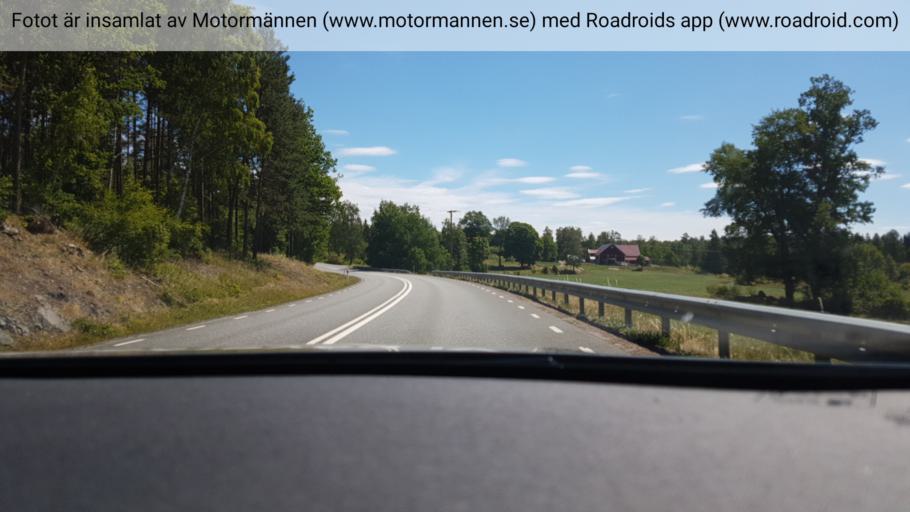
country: SE
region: Joenkoeping
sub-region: Jonkopings Kommun
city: Asa
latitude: 58.0095
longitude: 14.5351
